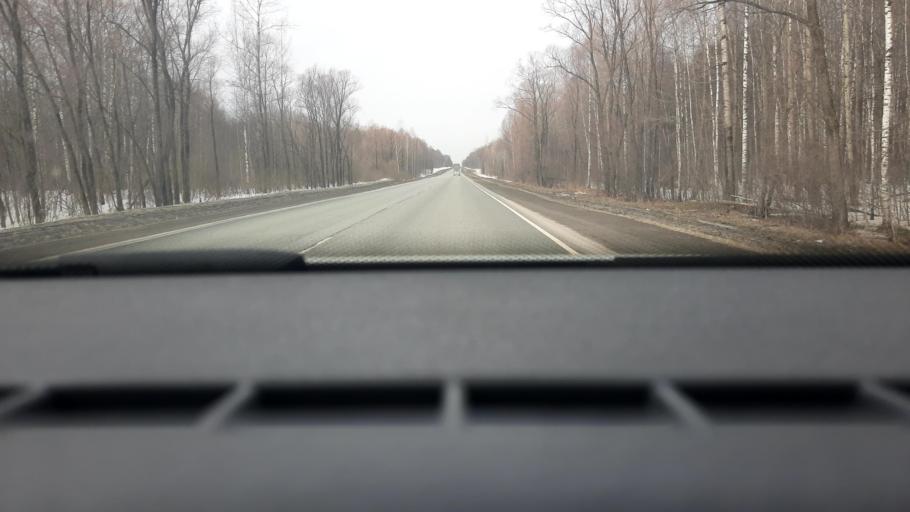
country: RU
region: Chelyabinsk
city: Asha
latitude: 54.8811
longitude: 57.2466
